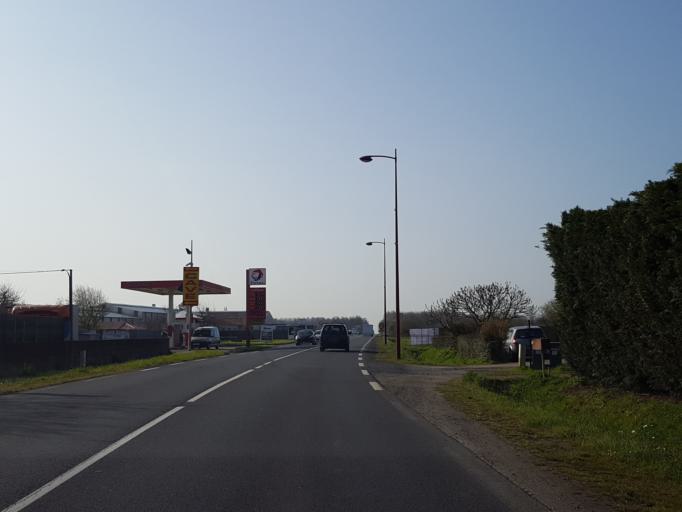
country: FR
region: Pays de la Loire
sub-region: Departement de la Loire-Atlantique
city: Geneston
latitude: 47.0512
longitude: -1.5093
